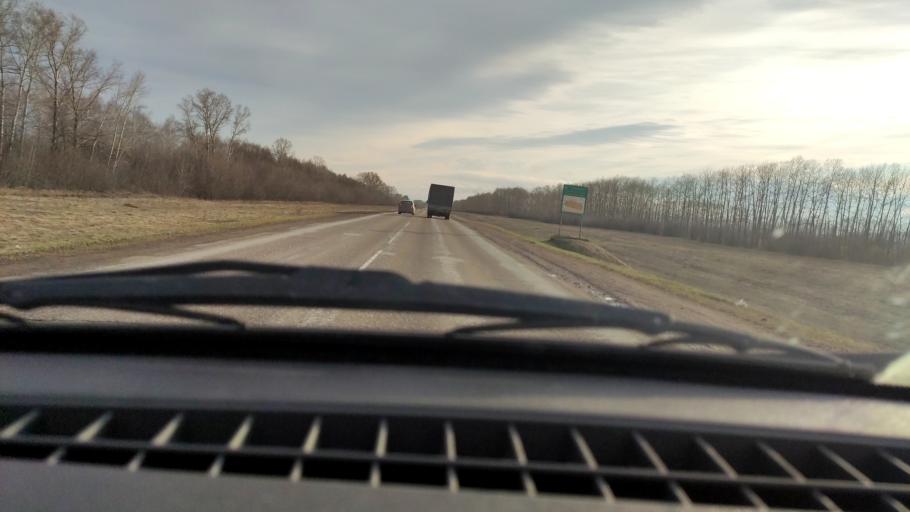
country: RU
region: Bashkortostan
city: Davlekanovo
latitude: 54.3605
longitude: 55.1932
